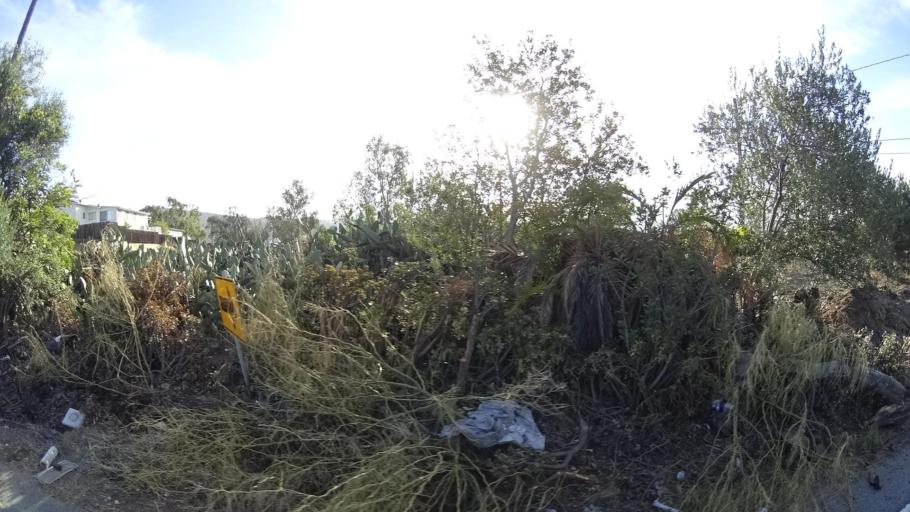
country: US
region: California
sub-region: San Diego County
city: La Presa
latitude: 32.7205
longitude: -117.0087
